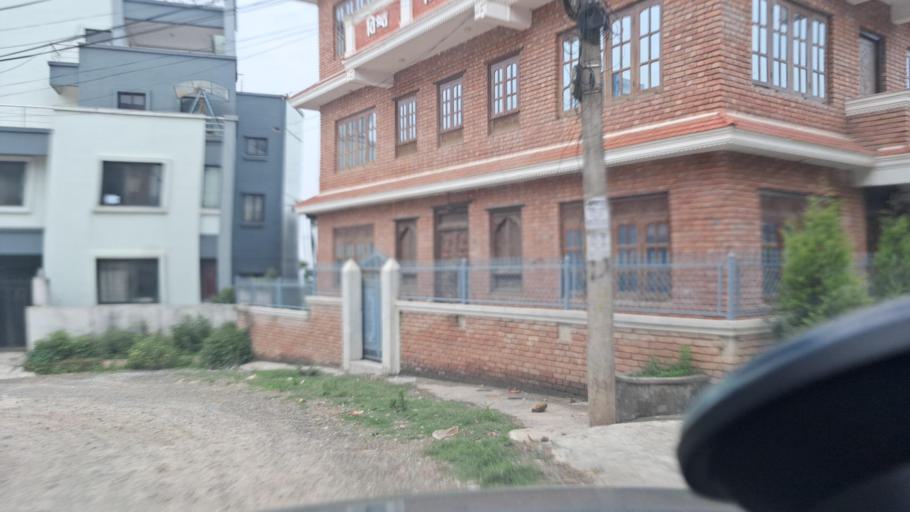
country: NP
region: Central Region
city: Banepa
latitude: 27.6155
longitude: 85.5524
